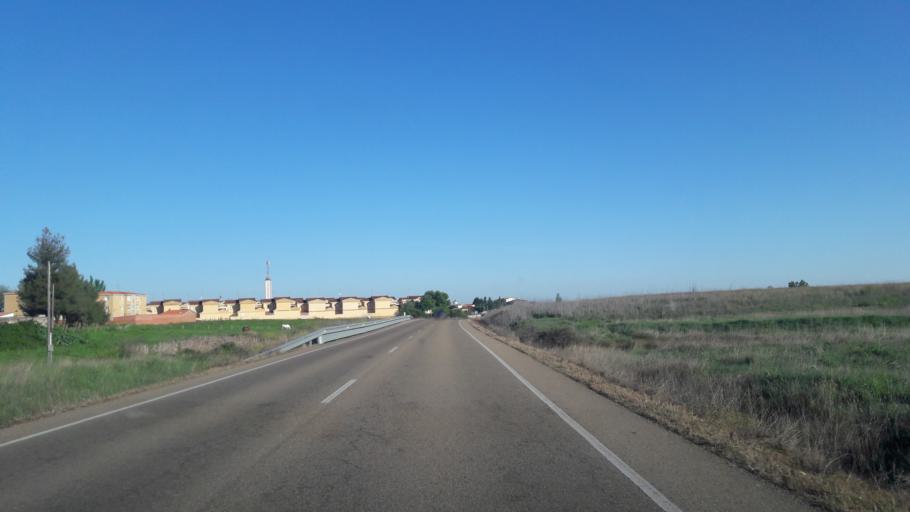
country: ES
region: Castille and Leon
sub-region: Provincia de Salamanca
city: La Fuente de San Esteban
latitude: 40.7979
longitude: -6.2509
